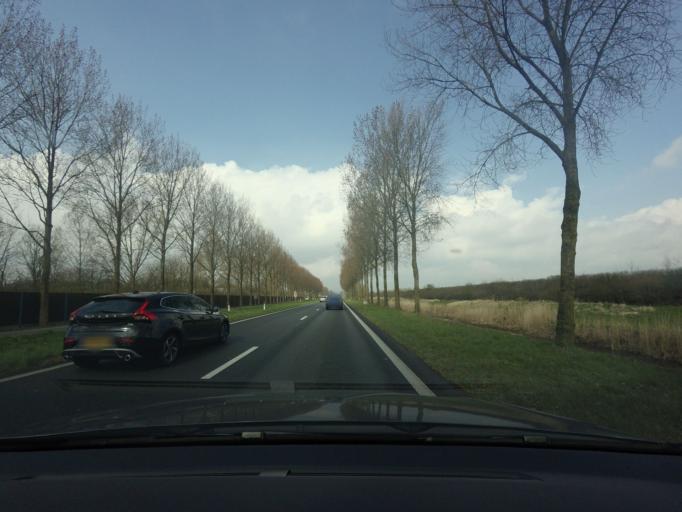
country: NL
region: North Holland
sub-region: Gemeente Haarlemmermeer
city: Hoofddorp
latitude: 52.3080
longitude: 4.7106
